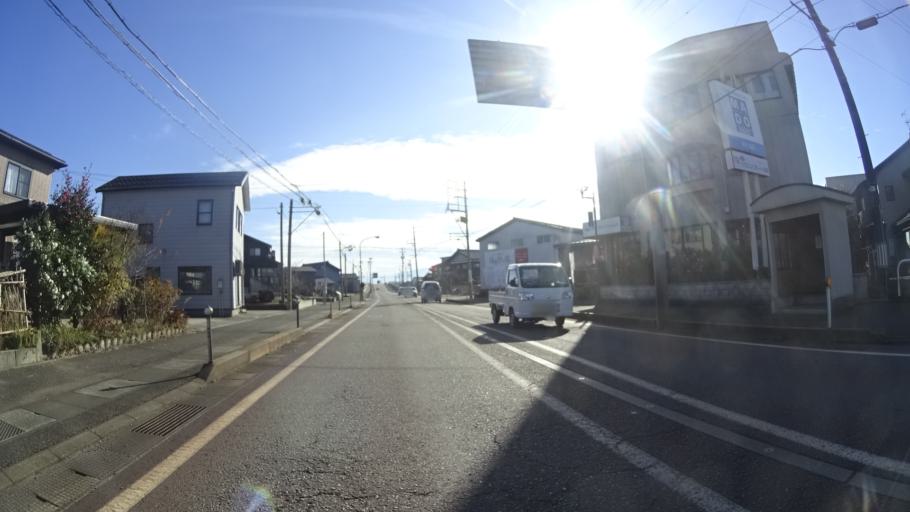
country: JP
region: Niigata
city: Mitsuke
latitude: 37.5473
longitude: 138.8775
